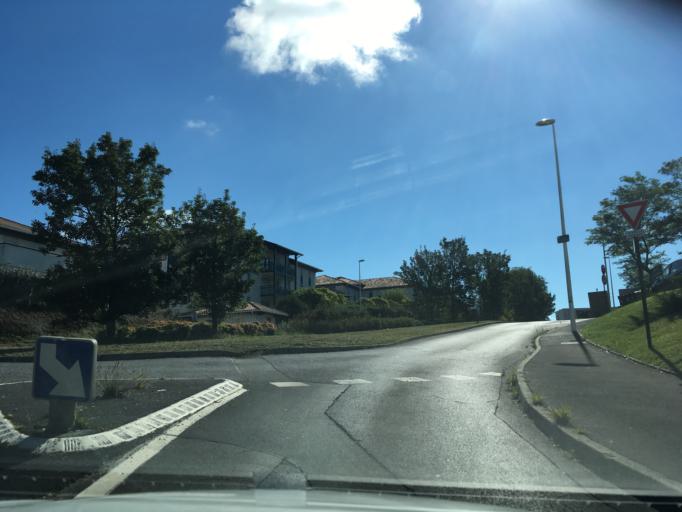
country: FR
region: Aquitaine
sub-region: Departement des Pyrenees-Atlantiques
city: Bayonne
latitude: 43.5077
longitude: -1.4812
